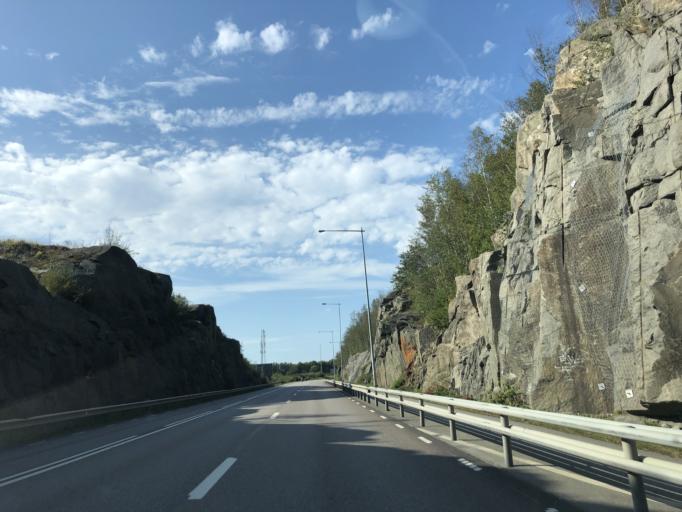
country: SE
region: Vaestra Goetaland
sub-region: Goteborg
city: Majorna
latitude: 57.7116
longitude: 11.8654
